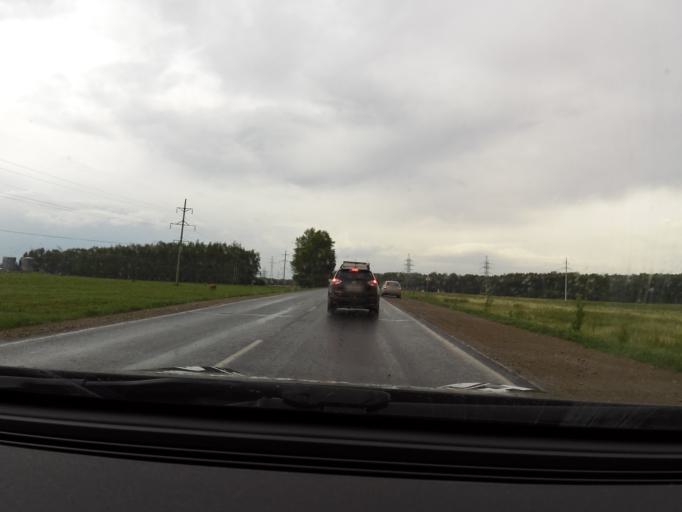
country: RU
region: Bashkortostan
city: Mikhaylovka
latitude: 54.8340
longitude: 55.8097
